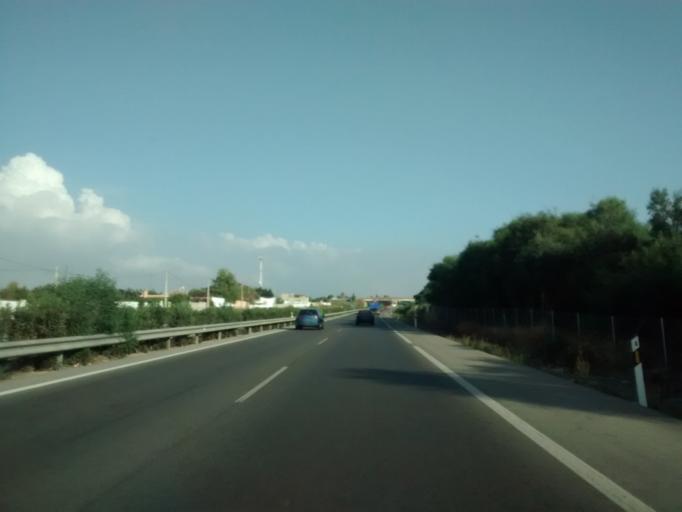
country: ES
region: Andalusia
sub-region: Provincia de Cadiz
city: Chiclana de la Frontera
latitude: 36.4396
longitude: -6.1275
